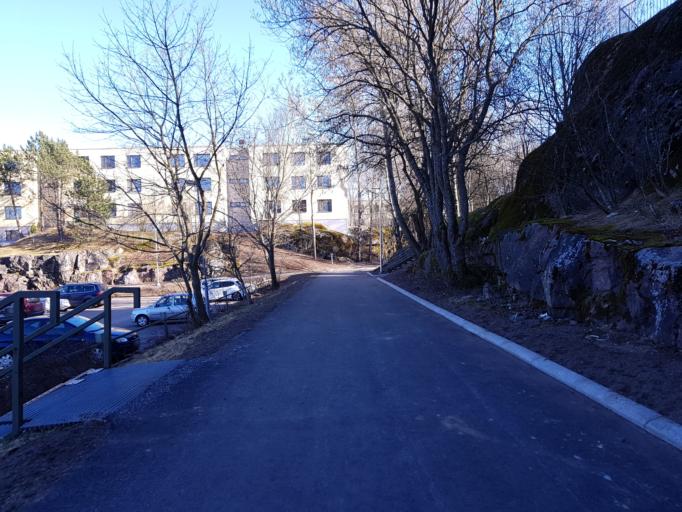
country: FI
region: Uusimaa
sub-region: Helsinki
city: Vantaa
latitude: 60.2310
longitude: 25.0023
